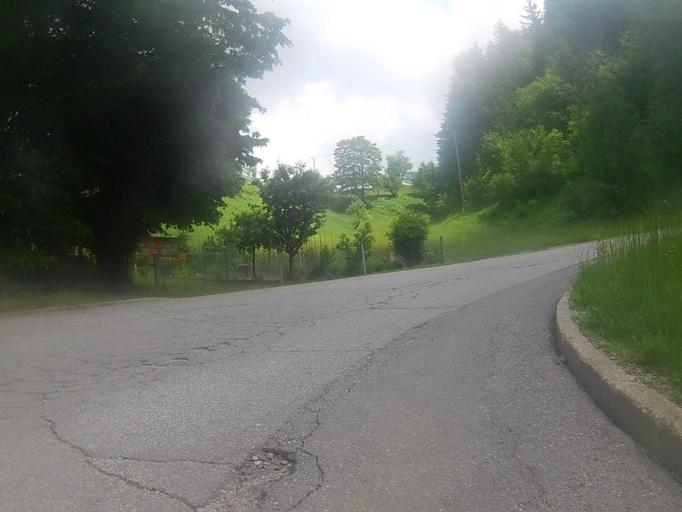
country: SI
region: Maribor
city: Bresternica
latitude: 46.6192
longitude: 15.5561
